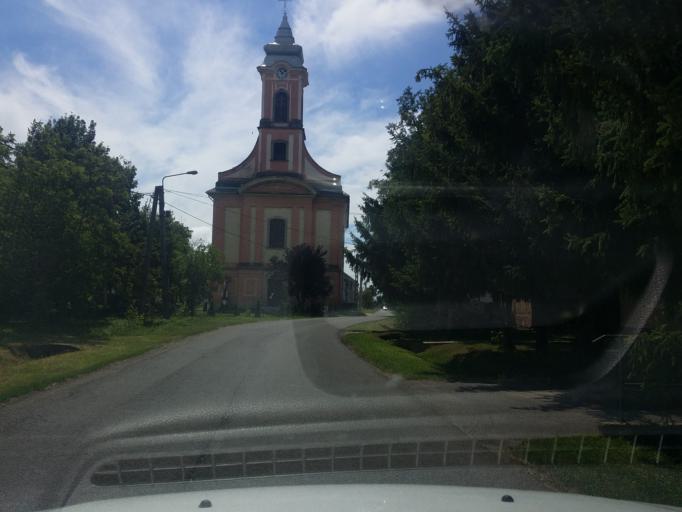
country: HU
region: Heves
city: Tiszanana
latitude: 47.5888
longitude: 20.5962
